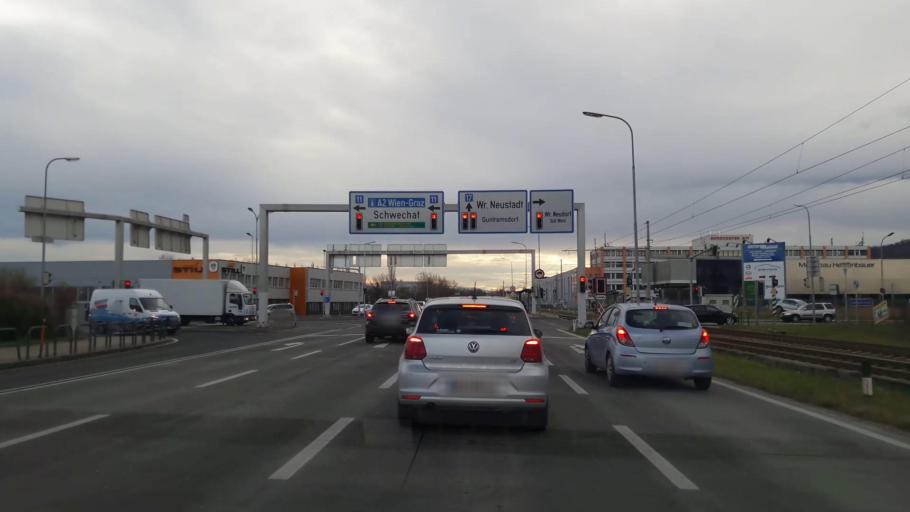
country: AT
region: Lower Austria
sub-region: Politischer Bezirk Modling
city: Wiener Neudorf
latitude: 48.0784
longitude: 16.3129
